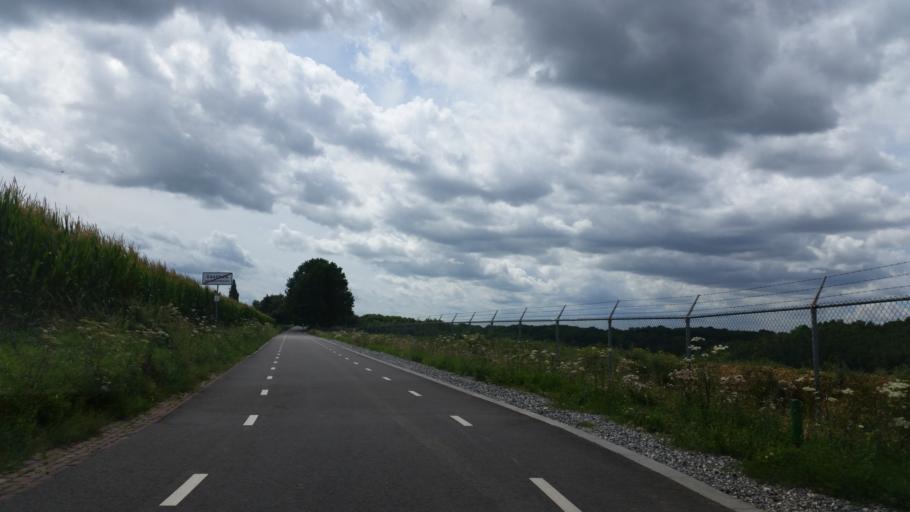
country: NL
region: Limburg
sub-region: Valkenburg aan de Geul
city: Berg
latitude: 50.8422
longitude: 5.7875
